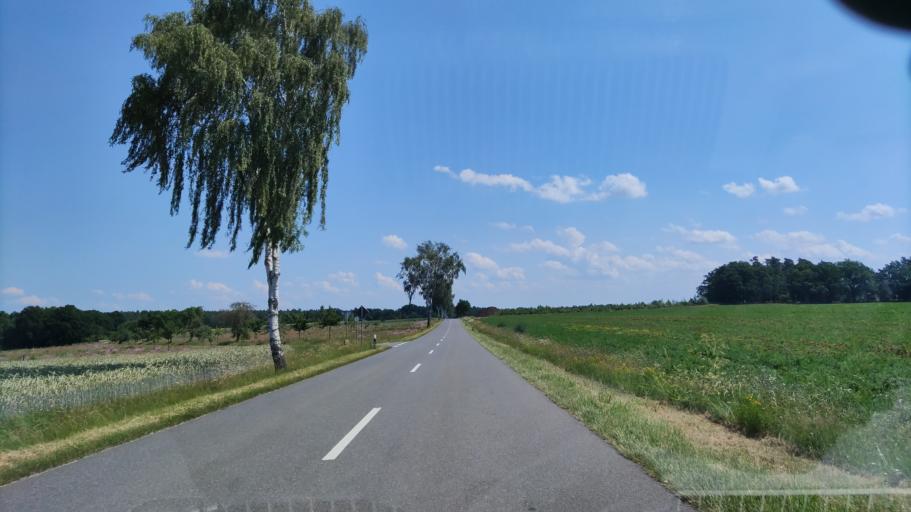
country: DE
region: Lower Saxony
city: Suderburg
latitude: 52.8810
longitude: 10.4158
